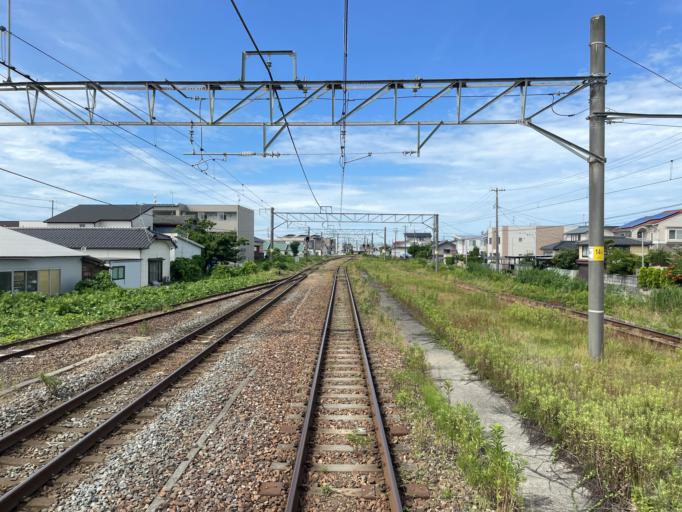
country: JP
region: Niigata
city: Suibara
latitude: 37.9186
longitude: 139.2144
